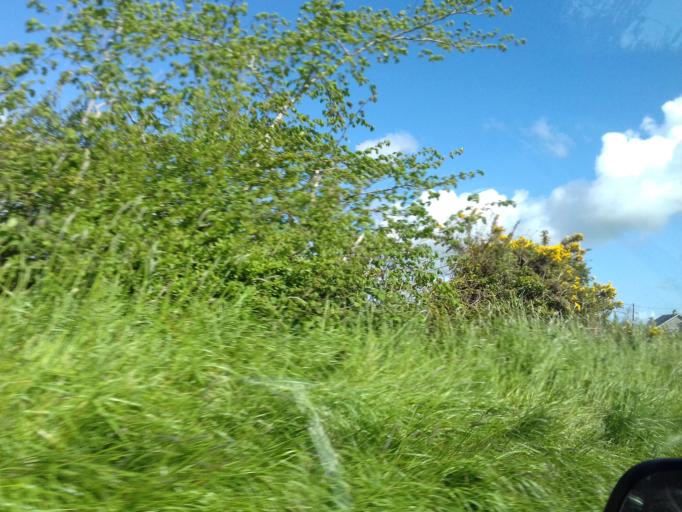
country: IE
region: Leinster
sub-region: Loch Garman
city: Castlebridge
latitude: 52.3889
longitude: -6.4078
